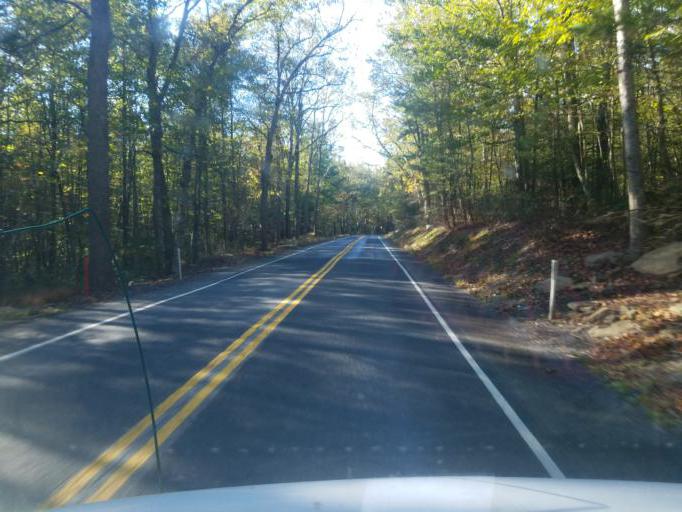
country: US
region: Pennsylvania
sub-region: Franklin County
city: Mont Alto
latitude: 39.8703
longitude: -77.4970
